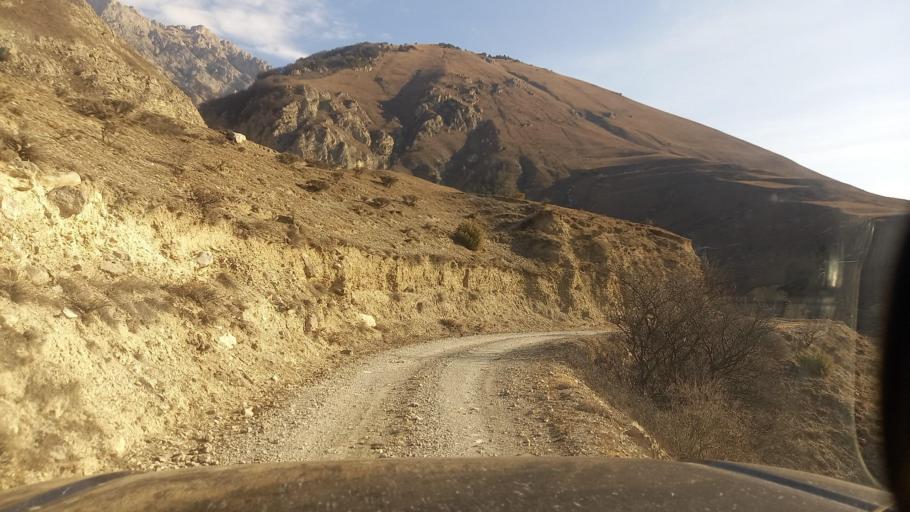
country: RU
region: Ingushetiya
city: Dzhayrakh
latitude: 42.8453
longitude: 44.6598
